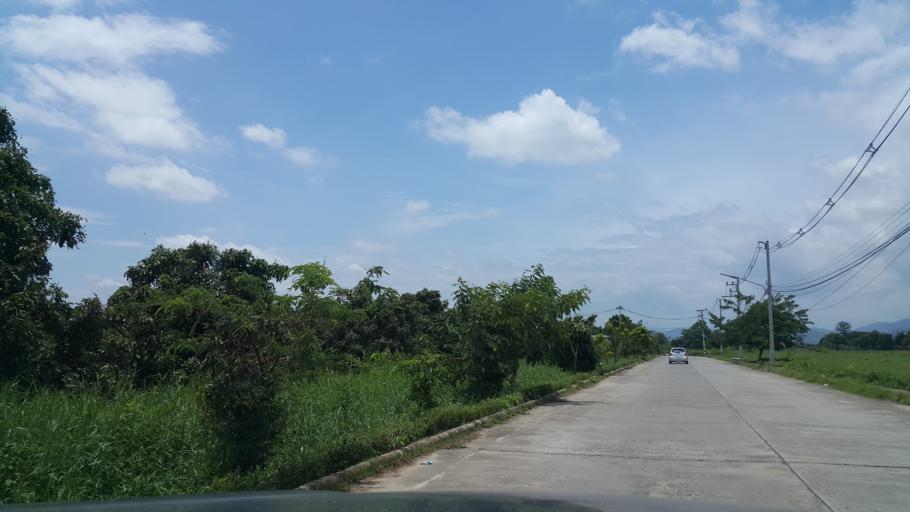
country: TH
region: Chiang Mai
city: Saraphi
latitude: 18.7089
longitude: 98.9762
